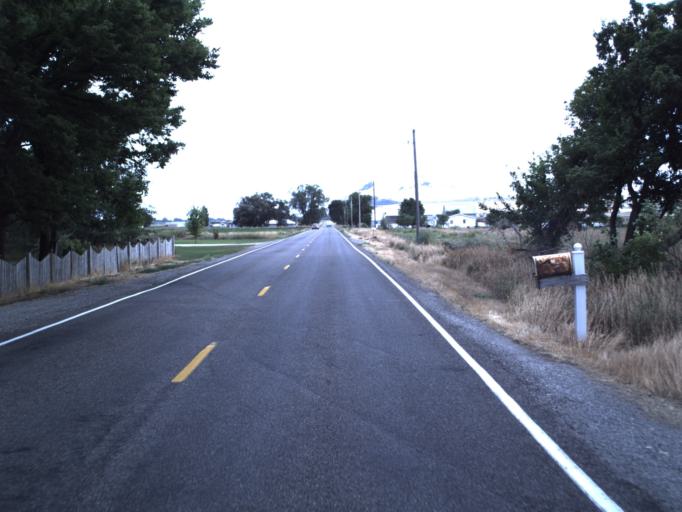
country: US
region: Utah
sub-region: Cache County
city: Lewiston
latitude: 41.9645
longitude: -111.9541
